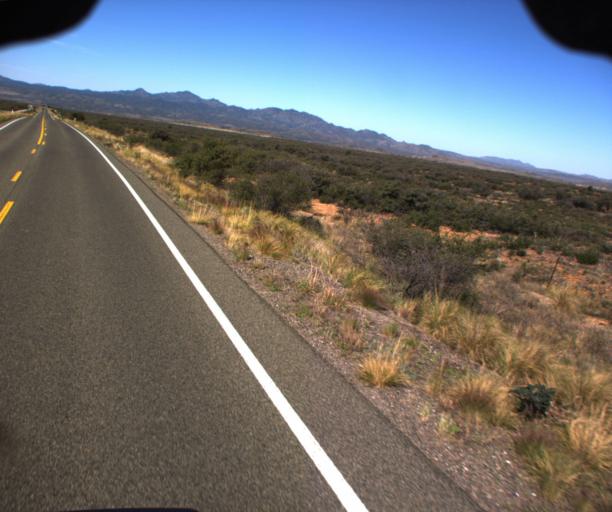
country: US
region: Arizona
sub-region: Yavapai County
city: Prescott
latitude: 34.4096
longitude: -112.6129
